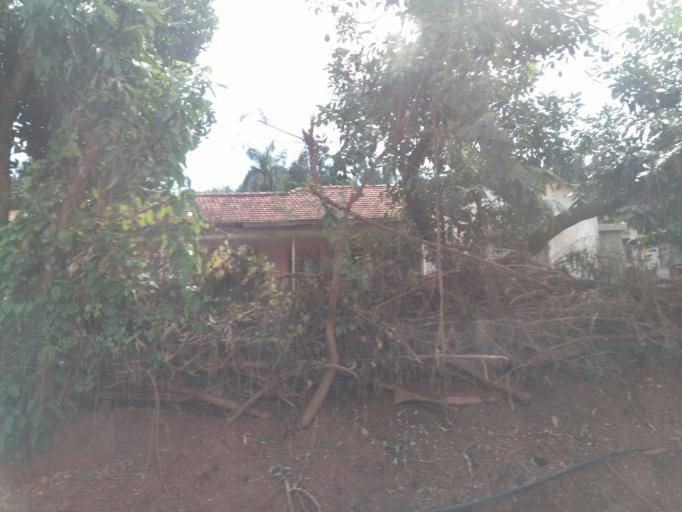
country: UG
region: Central Region
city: Kampala Central Division
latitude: 0.3454
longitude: 32.5645
